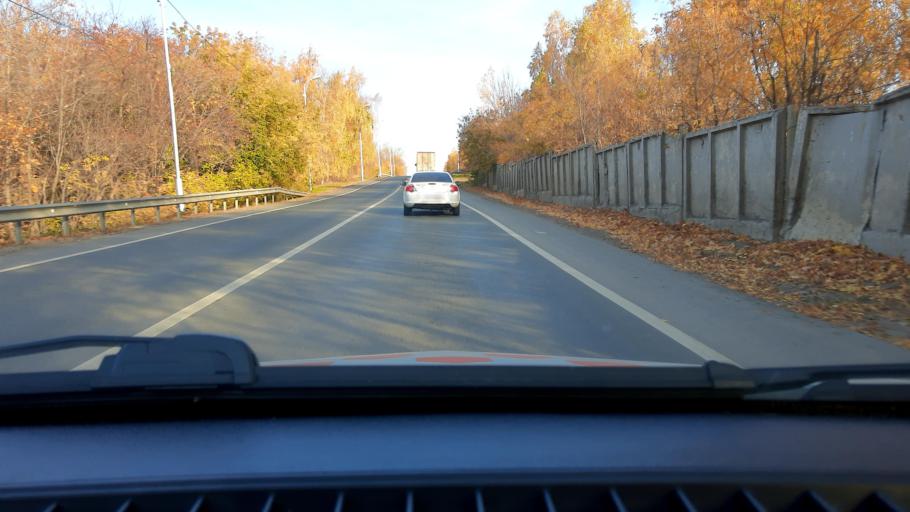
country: RU
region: Bashkortostan
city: Ufa
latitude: 54.8620
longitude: 56.0747
